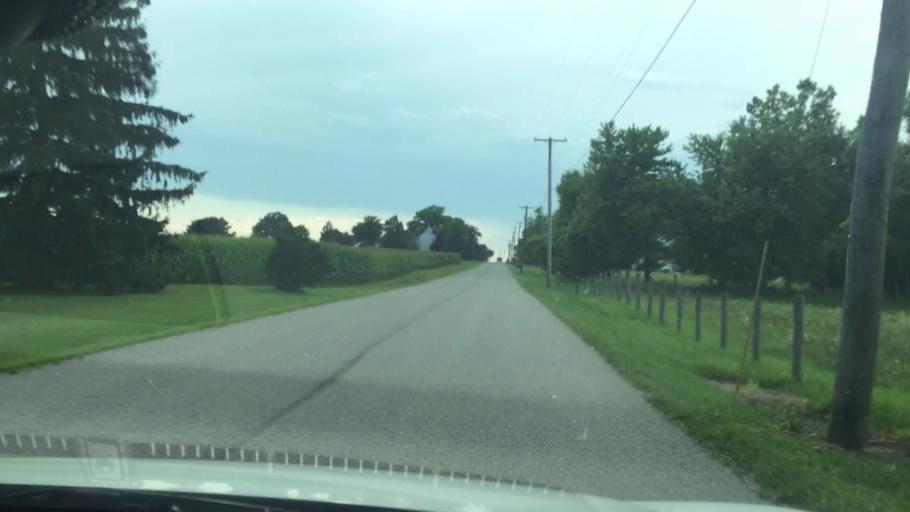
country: US
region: Ohio
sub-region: Clark County
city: Lisbon
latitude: 39.9452
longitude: -83.6061
